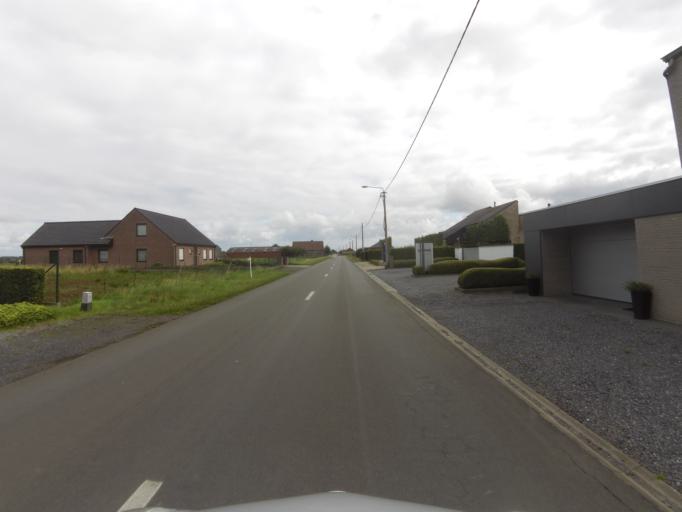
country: BE
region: Flanders
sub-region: Provincie West-Vlaanderen
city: Wingene
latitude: 51.0559
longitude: 3.2879
